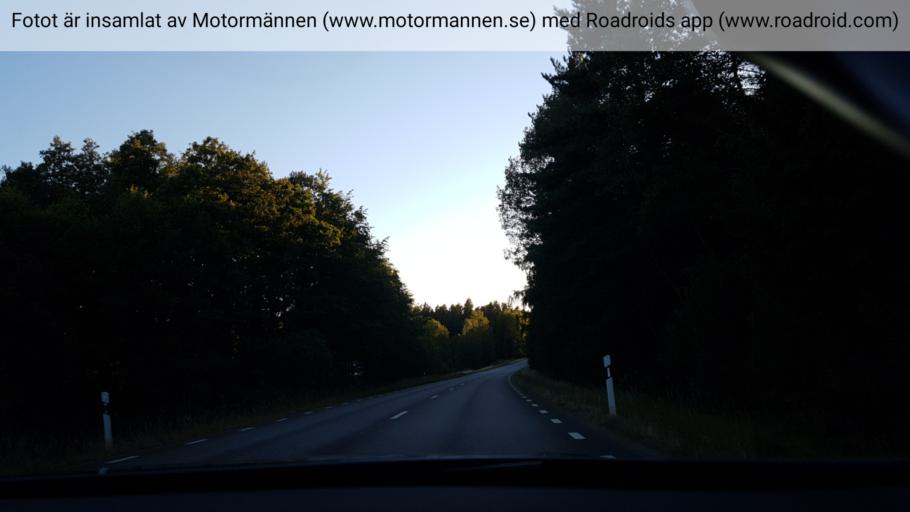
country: SE
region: Vaestra Goetaland
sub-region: Tibro Kommun
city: Tibro
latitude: 58.3420
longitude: 14.1666
